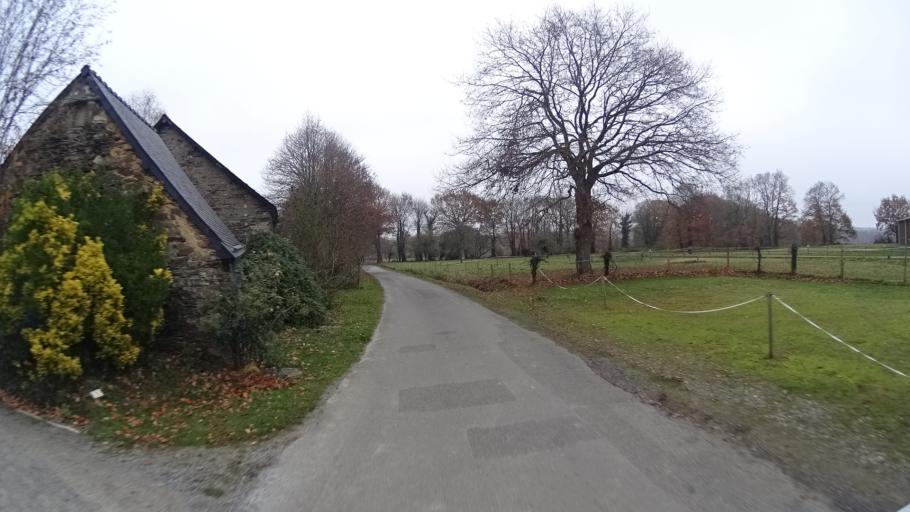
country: FR
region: Brittany
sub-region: Departement d'Ille-et-Vilaine
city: Bains-sur-Oust
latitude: 47.6909
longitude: -2.0725
